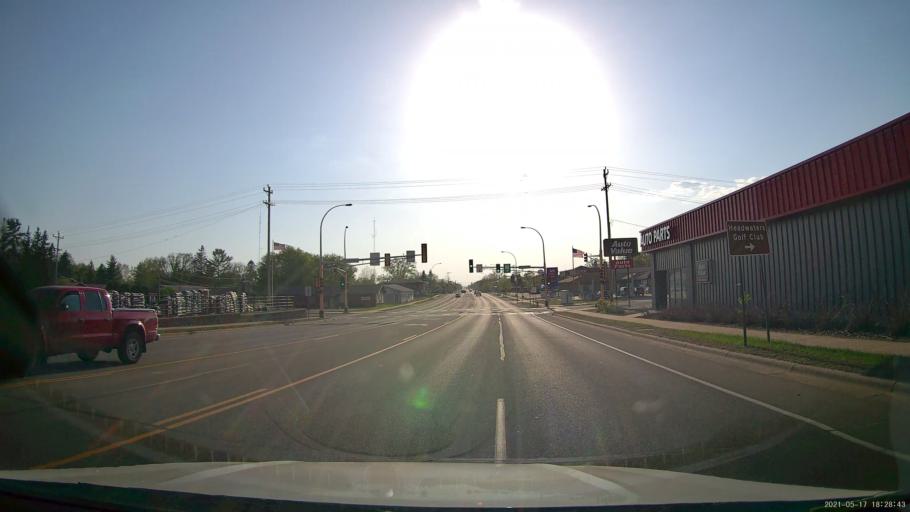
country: US
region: Minnesota
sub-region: Hubbard County
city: Park Rapids
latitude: 46.9222
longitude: -95.0470
